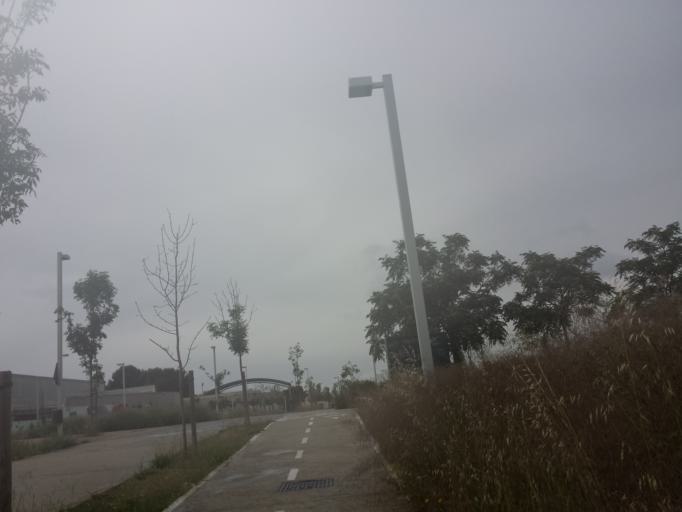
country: ES
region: Aragon
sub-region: Provincia de Zaragoza
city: Oliver-Valdefierro, Oliver, Valdefierro
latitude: 41.6382
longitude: -0.9225
